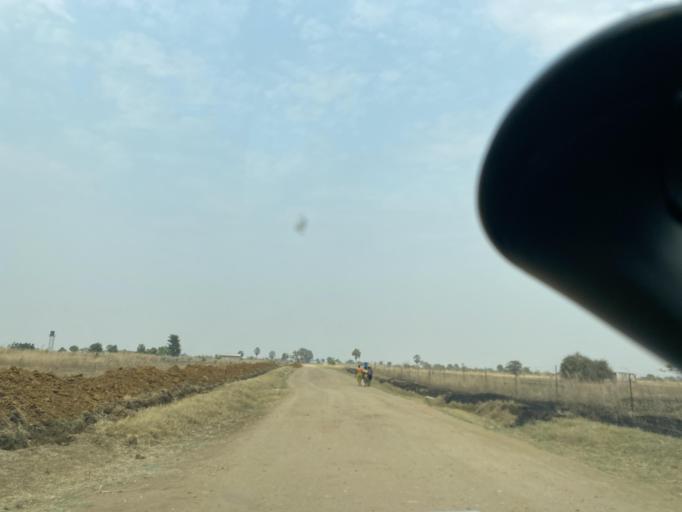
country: ZM
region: Lusaka
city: Kafue
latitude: -15.6457
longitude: 28.0804
